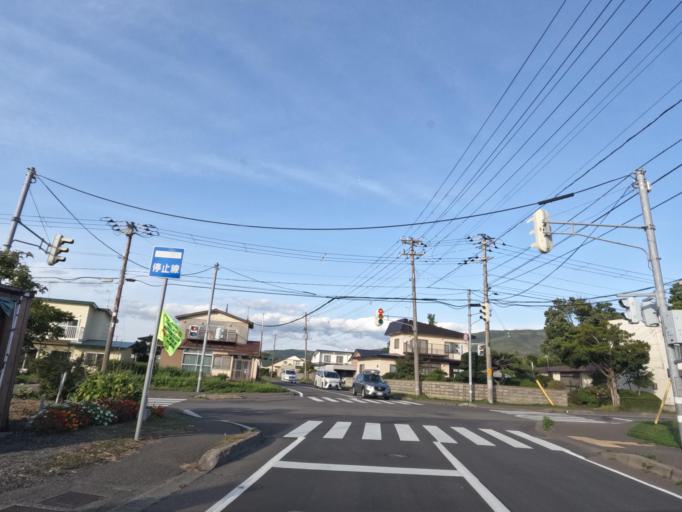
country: JP
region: Hokkaido
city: Date
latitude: 42.4667
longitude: 140.8843
